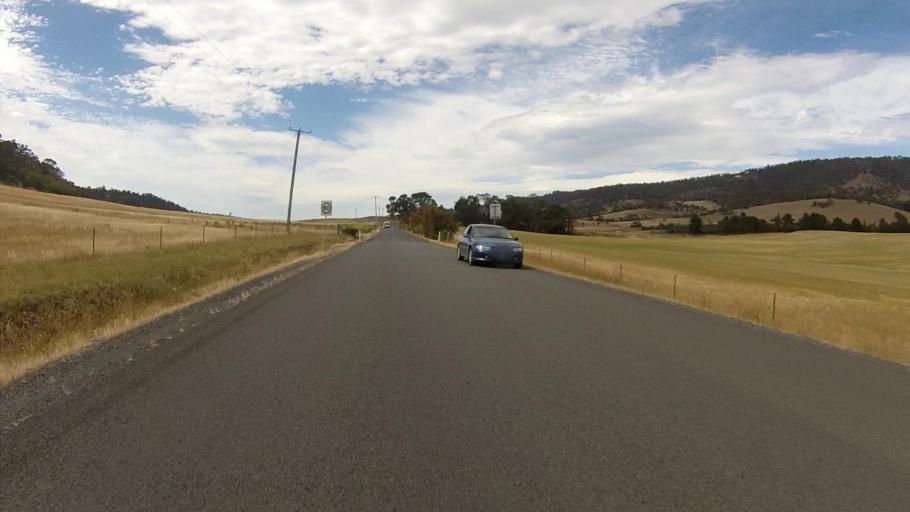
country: AU
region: Tasmania
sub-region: Brighton
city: Old Beach
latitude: -42.7247
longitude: 147.3422
